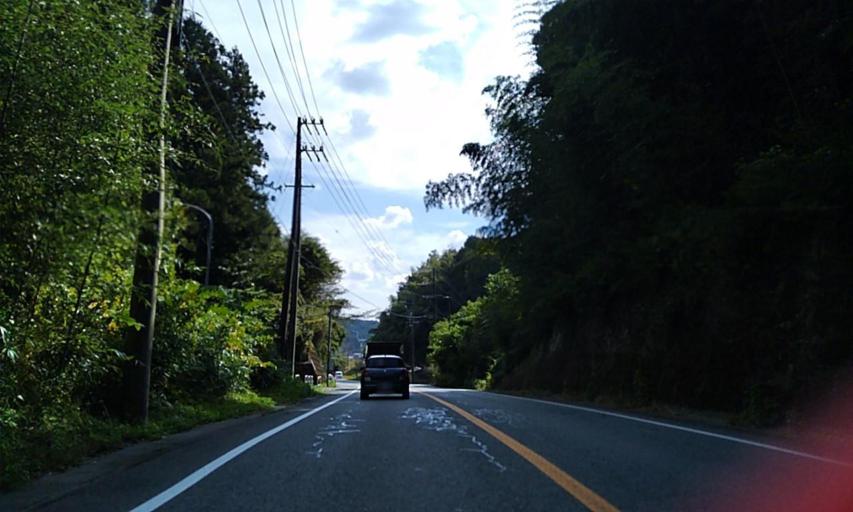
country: JP
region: Shizuoka
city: Mori
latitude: 34.8337
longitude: 137.8609
